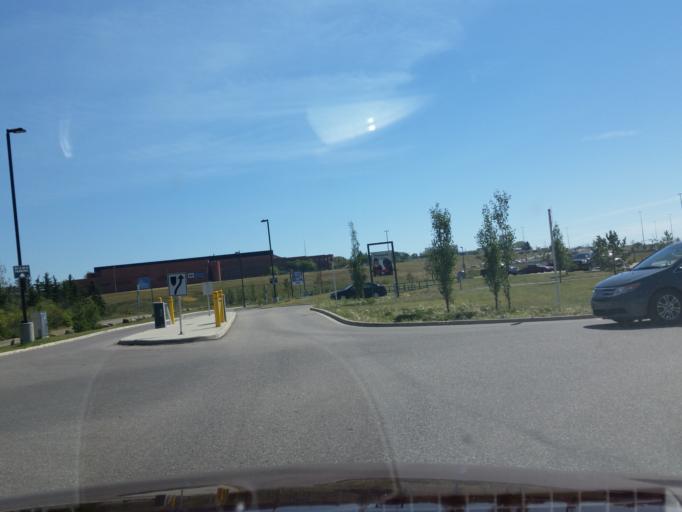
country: CA
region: Alberta
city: Calgary
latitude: 51.0510
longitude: -114.0244
